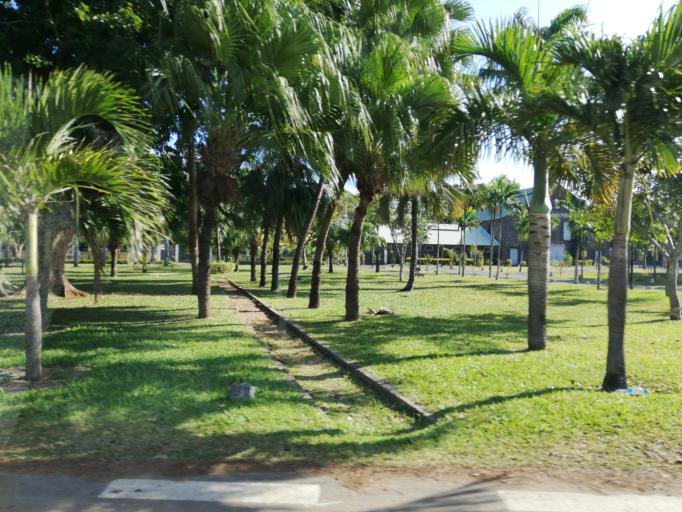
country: MU
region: Port Louis
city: Port Louis
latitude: -20.1590
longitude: 57.4888
